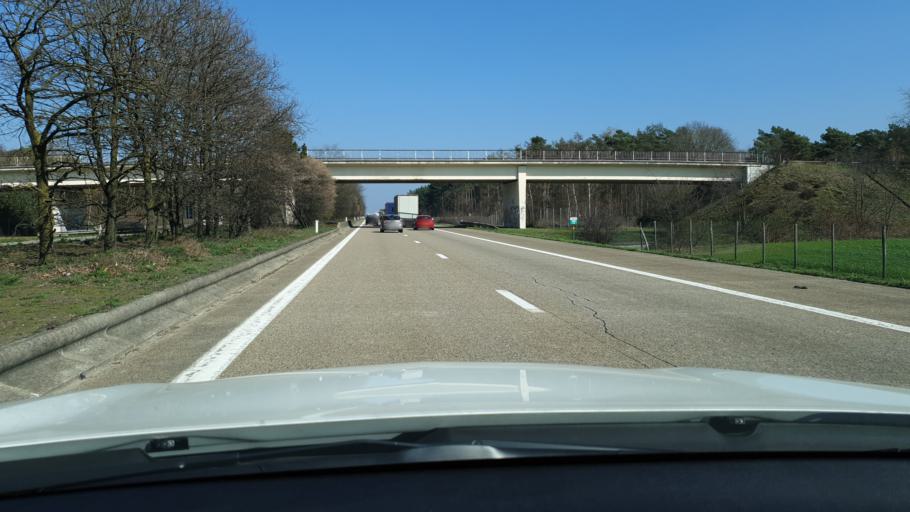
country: NL
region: North Brabant
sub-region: Gemeente Bladel en Netersel
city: Bladel
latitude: 51.3091
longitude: 5.1791
